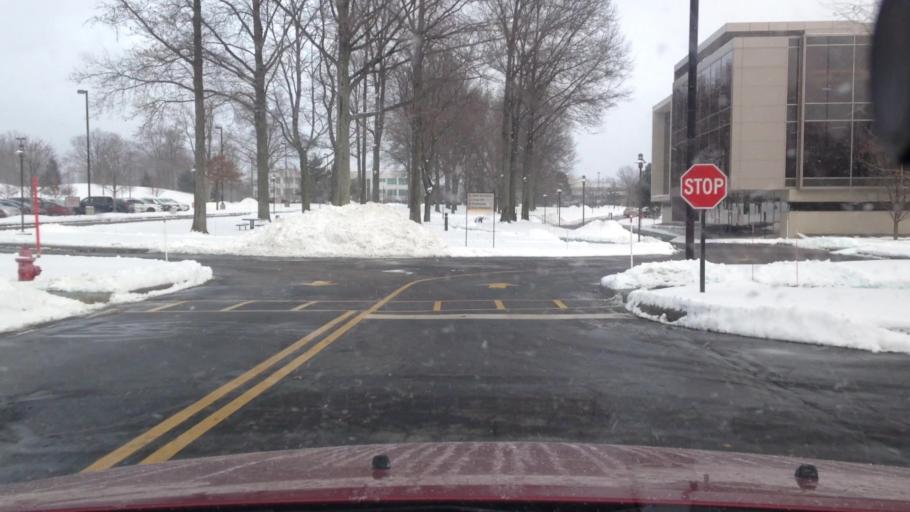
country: US
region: Ohio
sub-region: Cuyahoga County
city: Mayfield Heights
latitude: 41.5074
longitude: -81.4616
